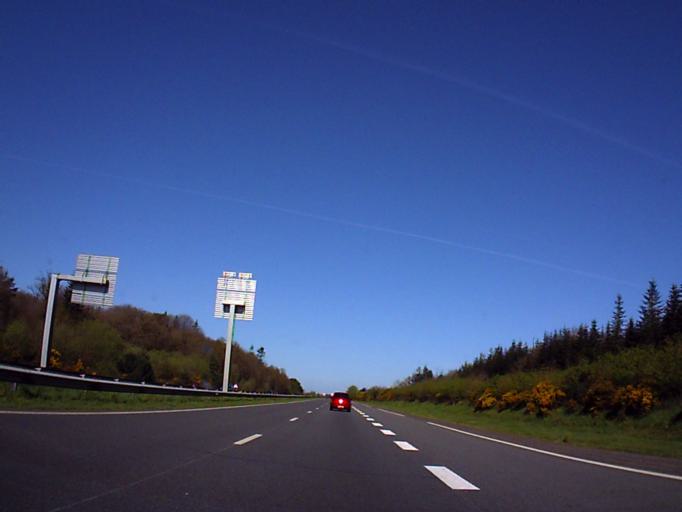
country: FR
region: Brittany
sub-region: Departement des Cotes-d'Armor
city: Plestan
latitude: 48.4084
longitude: -2.4205
